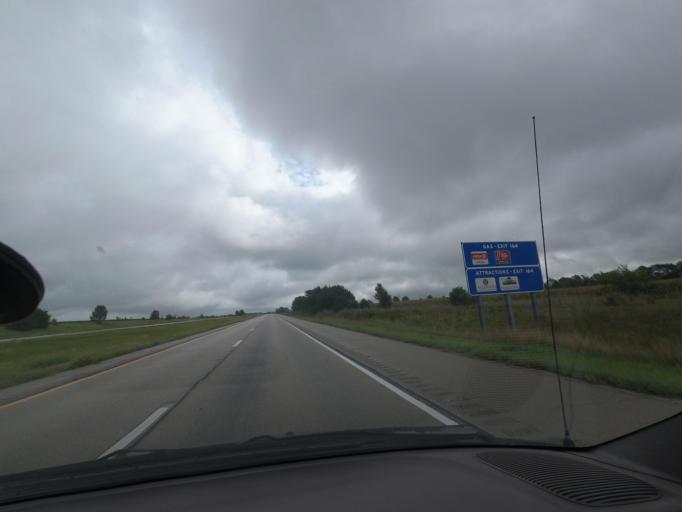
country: US
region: Illinois
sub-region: Piatt County
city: Monticello
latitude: 40.0309
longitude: -88.6222
